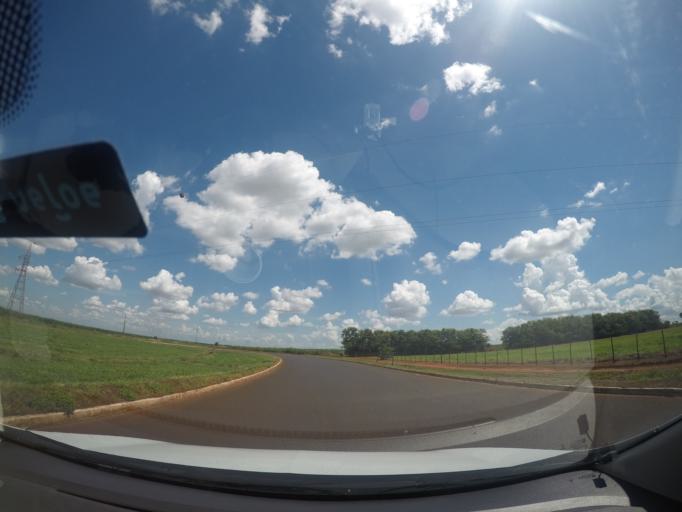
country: BR
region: Minas Gerais
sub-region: Frutal
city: Frutal
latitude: -19.8179
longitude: -48.7315
